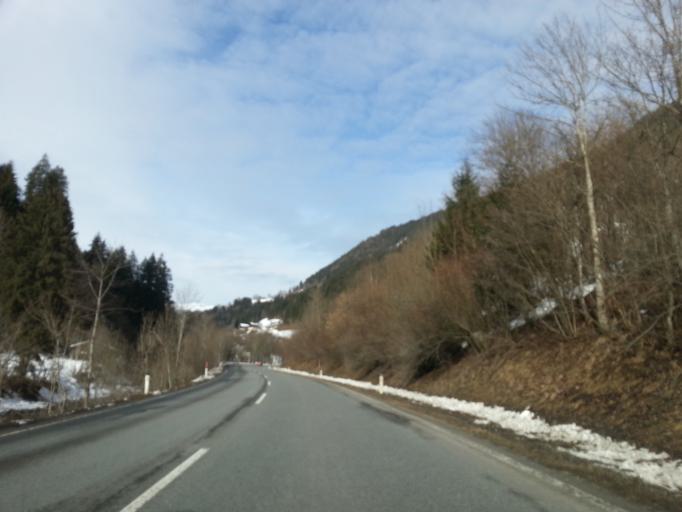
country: AT
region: Salzburg
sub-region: Politischer Bezirk Zell am See
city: Maishofen
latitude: 47.3653
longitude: 12.7771
